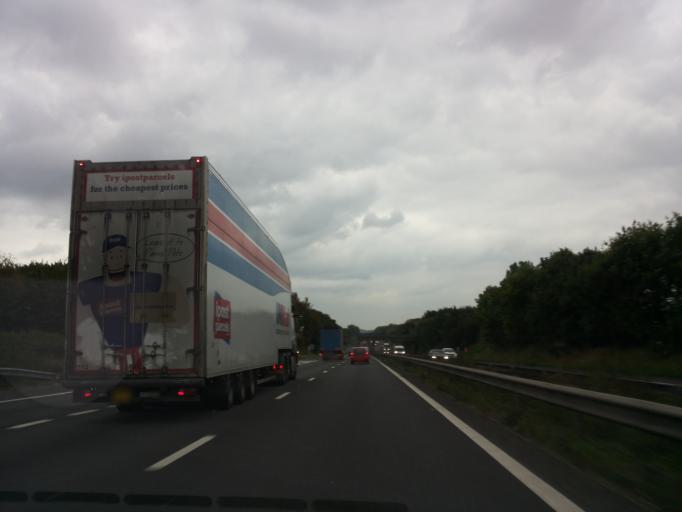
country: GB
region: England
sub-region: Kent
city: Faversham
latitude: 51.3011
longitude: 0.8845
